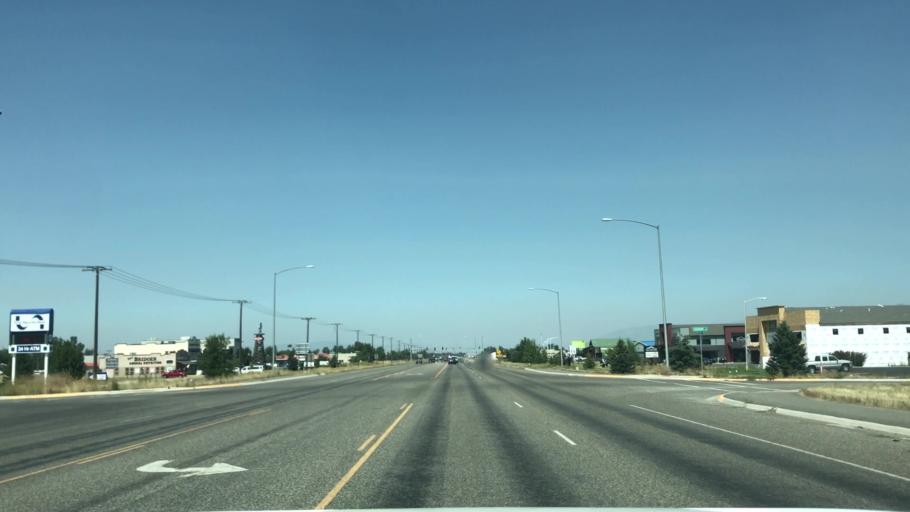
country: US
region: Montana
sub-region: Gallatin County
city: Four Corners
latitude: 45.6750
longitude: -111.1856
